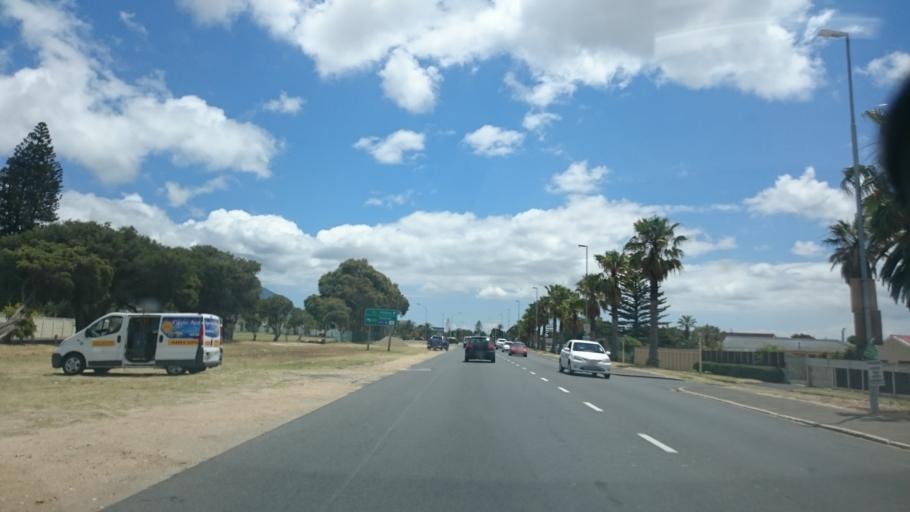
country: ZA
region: Western Cape
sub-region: City of Cape Town
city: Bergvliet
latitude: -34.0551
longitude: 18.4610
